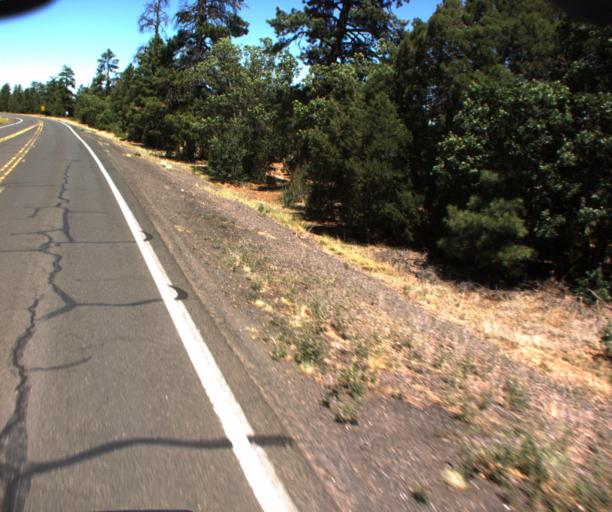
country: US
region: Arizona
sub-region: Gila County
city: Star Valley
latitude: 34.6500
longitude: -111.1086
